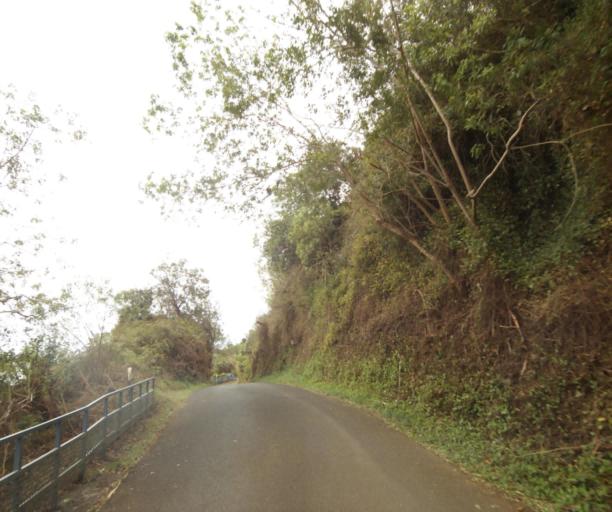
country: RE
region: Reunion
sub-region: Reunion
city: Saint-Paul
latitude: -21.0105
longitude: 55.3417
